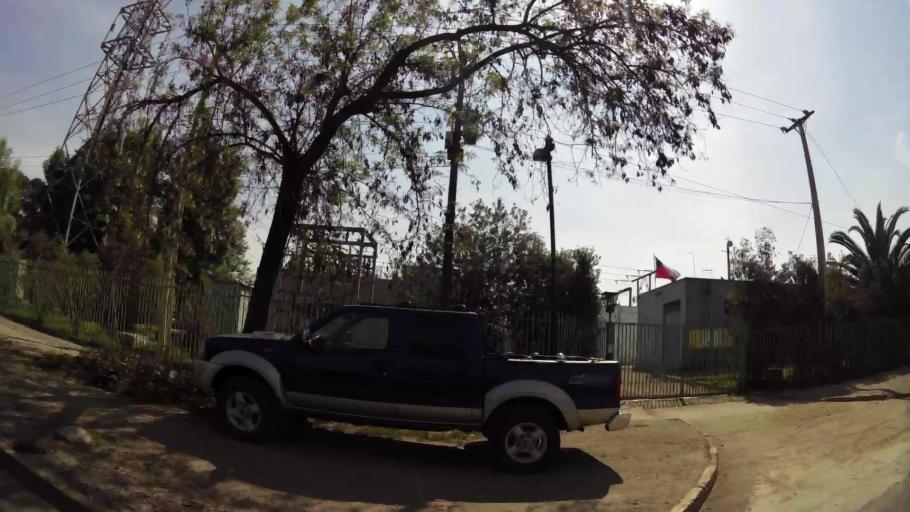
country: CL
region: Santiago Metropolitan
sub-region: Provincia de Santiago
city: Villa Presidente Frei, Nunoa, Santiago, Chile
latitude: -33.5067
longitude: -70.5746
